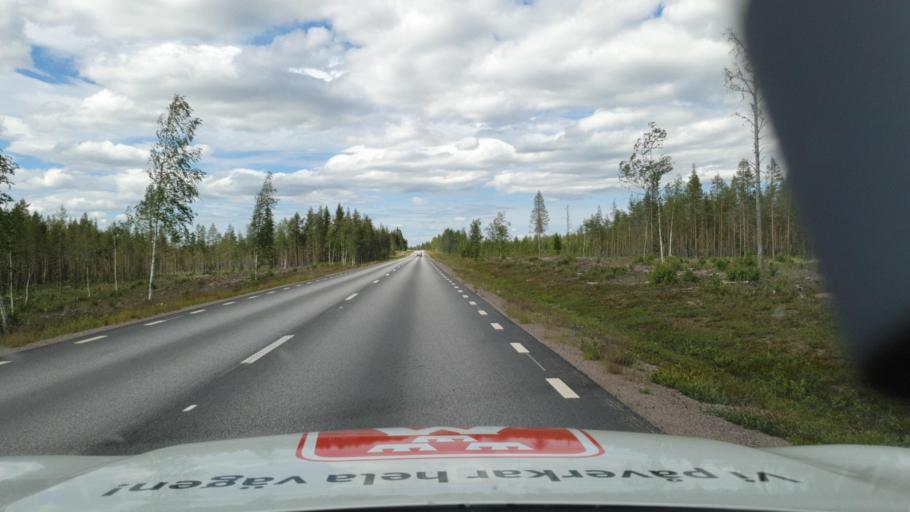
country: SE
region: Vaesterbotten
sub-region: Skelleftea Kommun
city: Langsele
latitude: 65.1174
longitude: 19.9554
